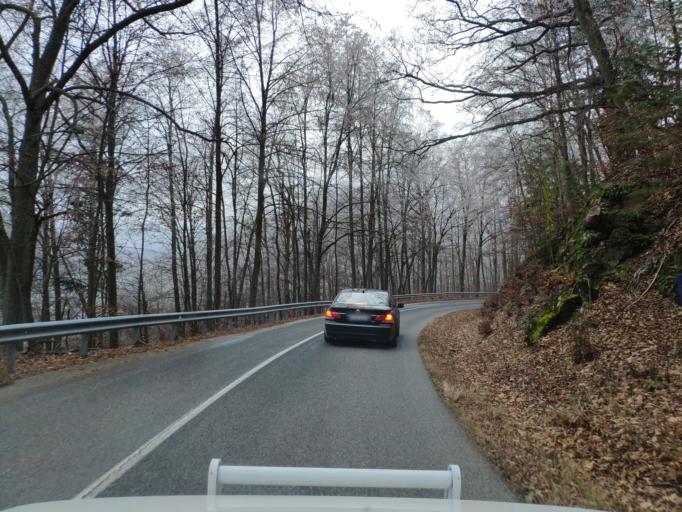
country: SK
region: Kosicky
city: Dobsina
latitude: 48.7945
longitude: 20.4824
